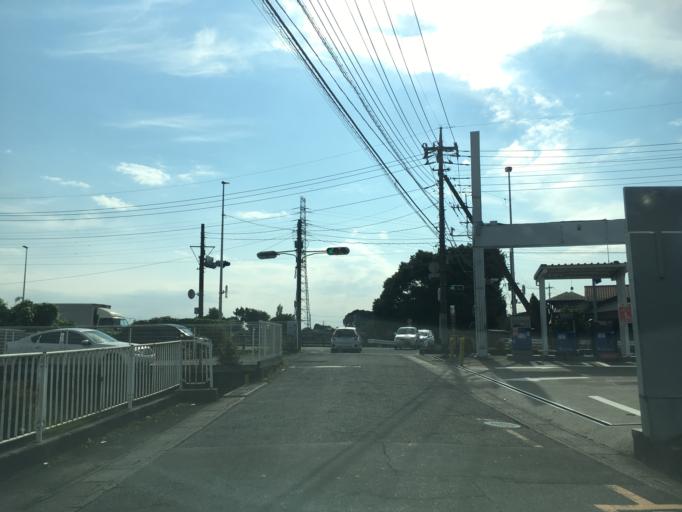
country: JP
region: Saitama
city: Iwatsuki
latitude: 35.9406
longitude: 139.6815
